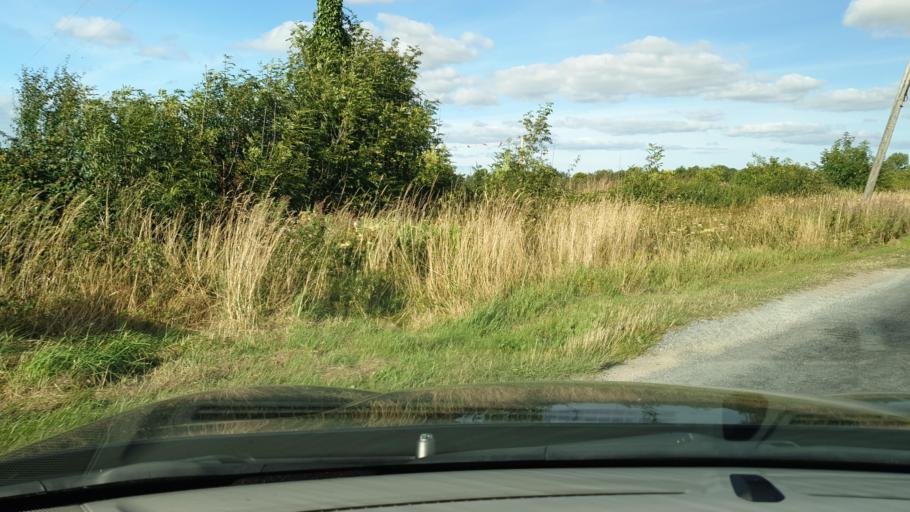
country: IE
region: Leinster
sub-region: An Mhi
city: Ashbourne
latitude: 53.4646
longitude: -6.4183
